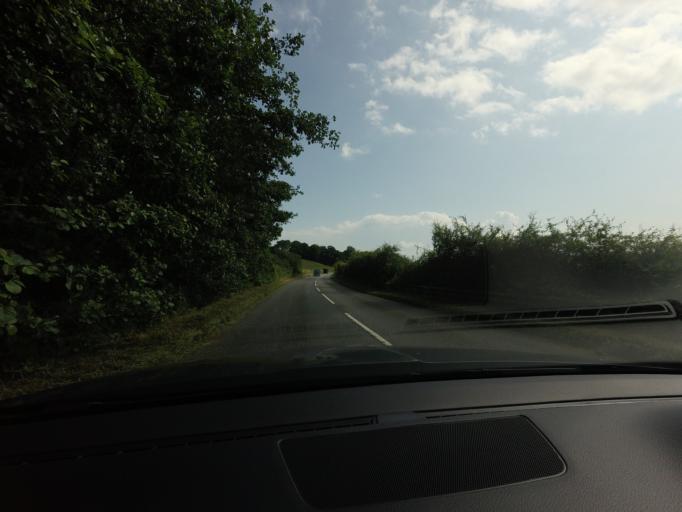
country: GB
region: Scotland
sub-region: Highland
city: Evanton
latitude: 57.6253
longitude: -4.3763
